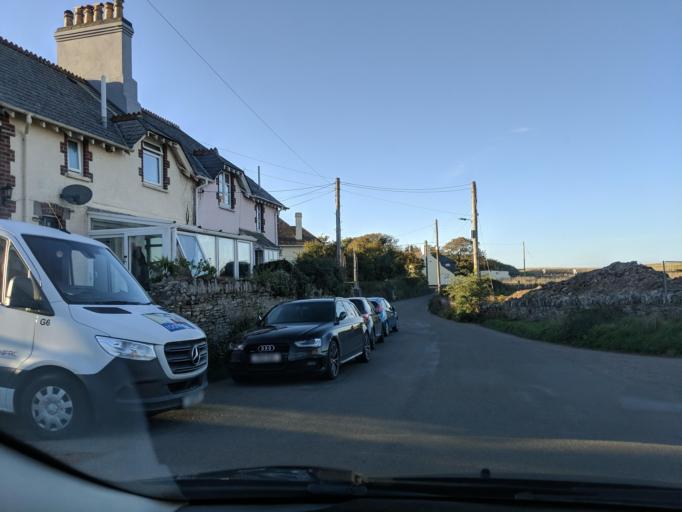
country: GB
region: England
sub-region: Devon
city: Wembury
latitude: 50.3325
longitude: -4.1039
